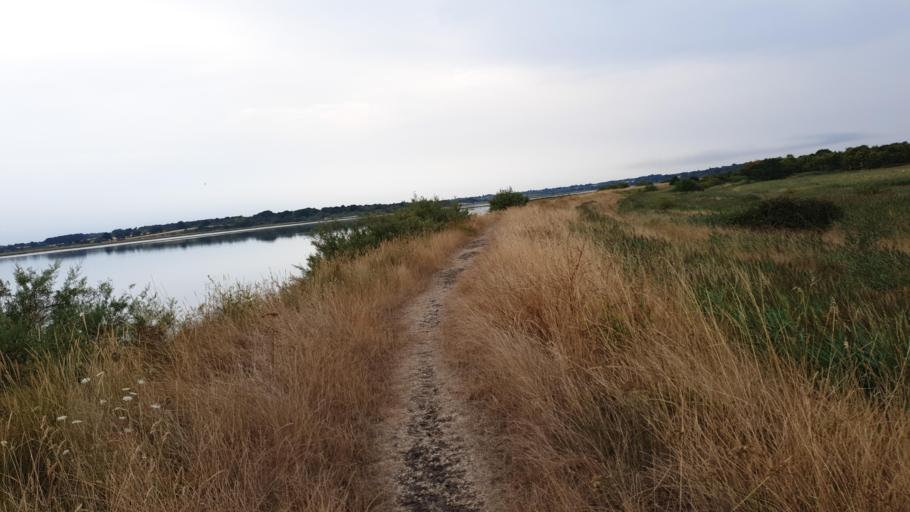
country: GB
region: England
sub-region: Essex
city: Alresford
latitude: 51.8247
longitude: 0.9867
